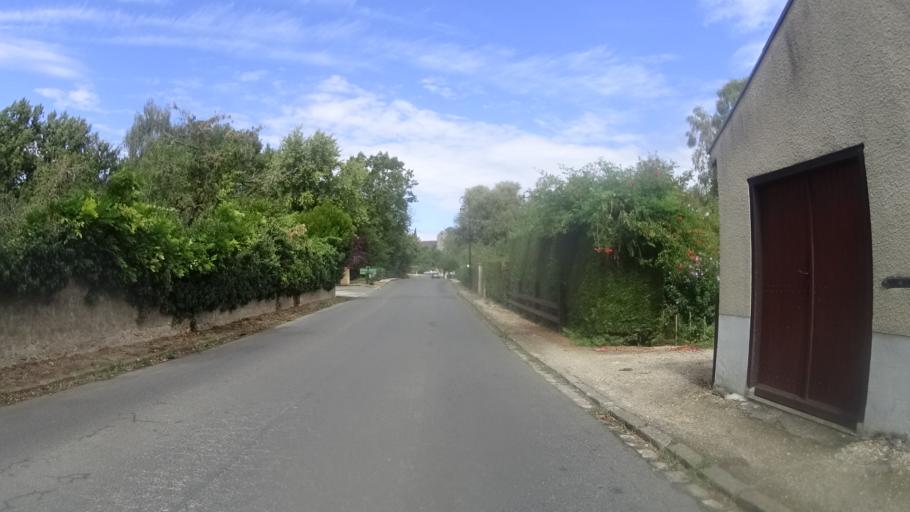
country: FR
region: Centre
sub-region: Departement du Loiret
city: Malesherbes
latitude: 48.2021
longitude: 2.4092
